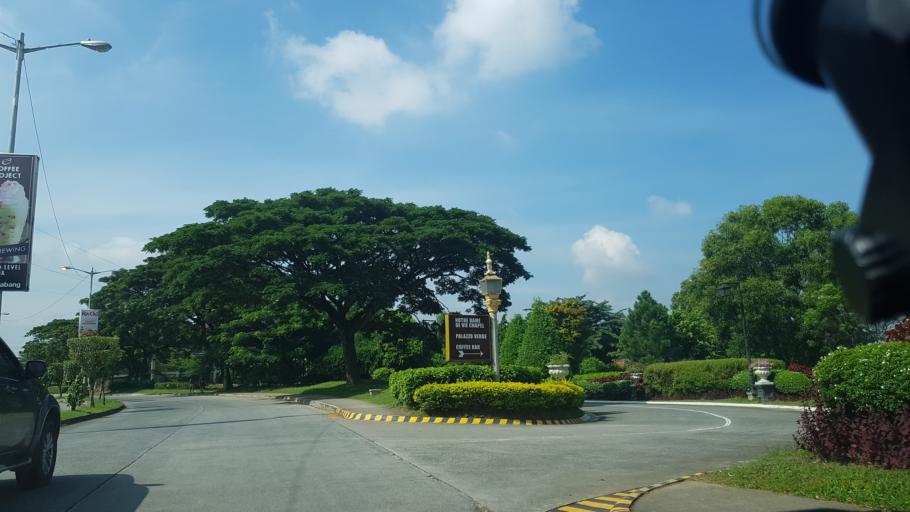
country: PH
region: Calabarzon
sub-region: Province of Laguna
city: San Pedro
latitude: 14.3703
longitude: 121.0102
